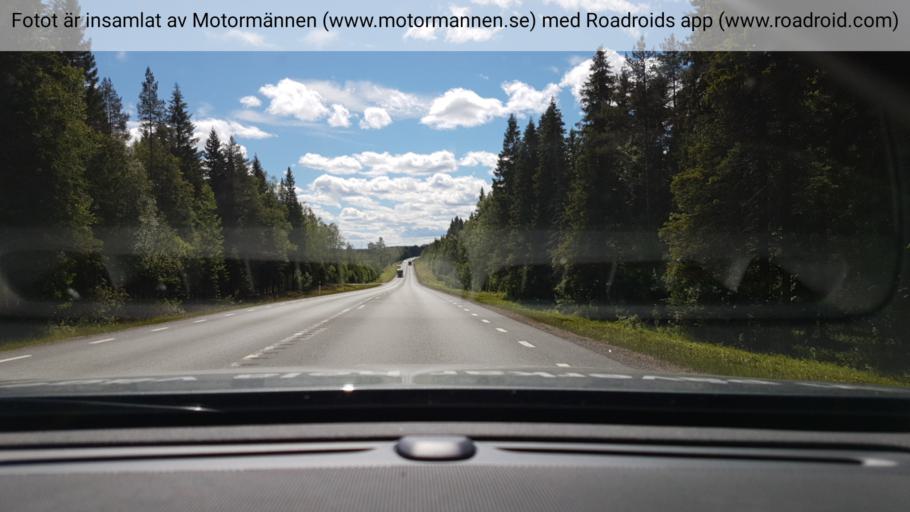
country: SE
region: Vaesterbotten
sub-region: Skelleftea Kommun
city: Burea
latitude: 64.3590
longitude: 21.2959
